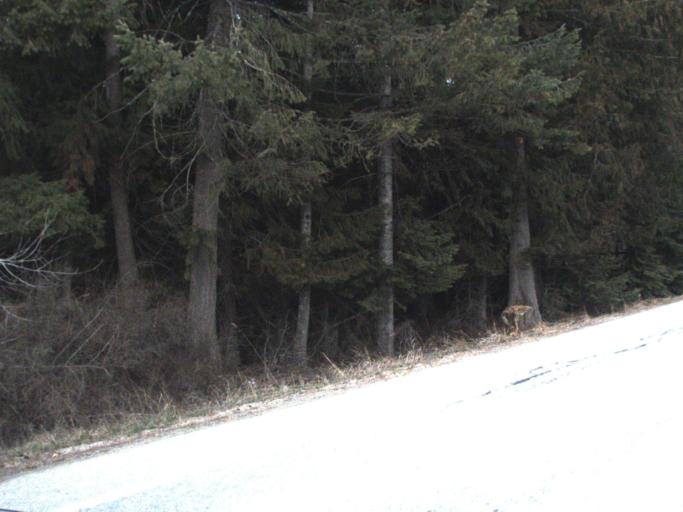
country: US
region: Washington
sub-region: Pend Oreille County
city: Newport
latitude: 48.1966
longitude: -117.0574
